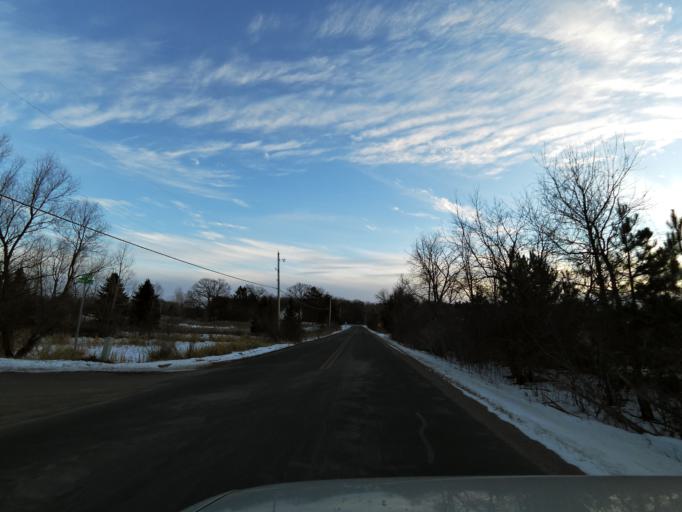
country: US
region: Minnesota
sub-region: Washington County
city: Lake Elmo
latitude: 44.9805
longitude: -92.8430
